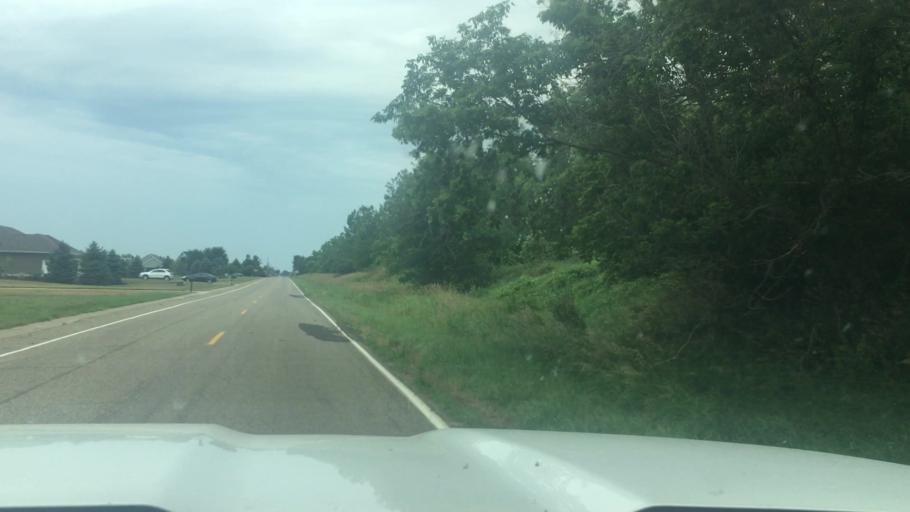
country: US
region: Michigan
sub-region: Clinton County
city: Saint Johns
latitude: 43.0509
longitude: -84.4842
